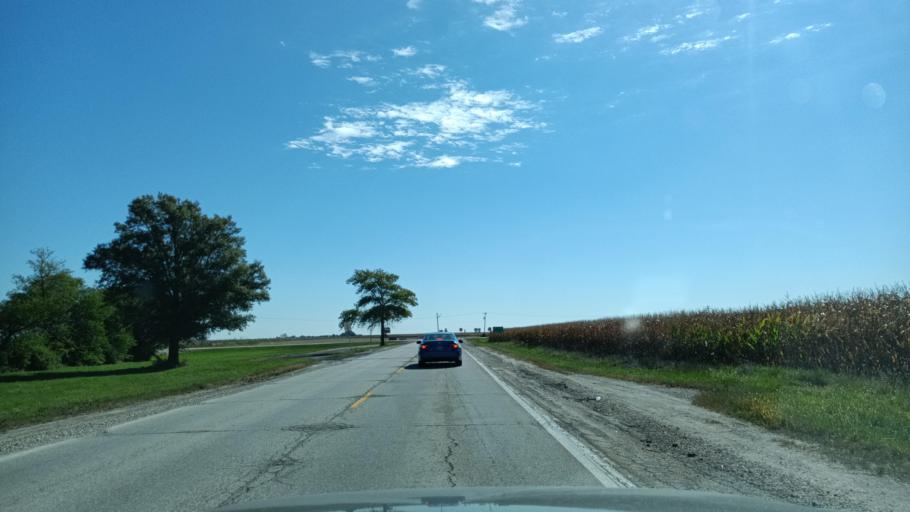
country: US
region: Illinois
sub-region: Knox County
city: Knoxville
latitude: 40.9069
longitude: -90.2531
